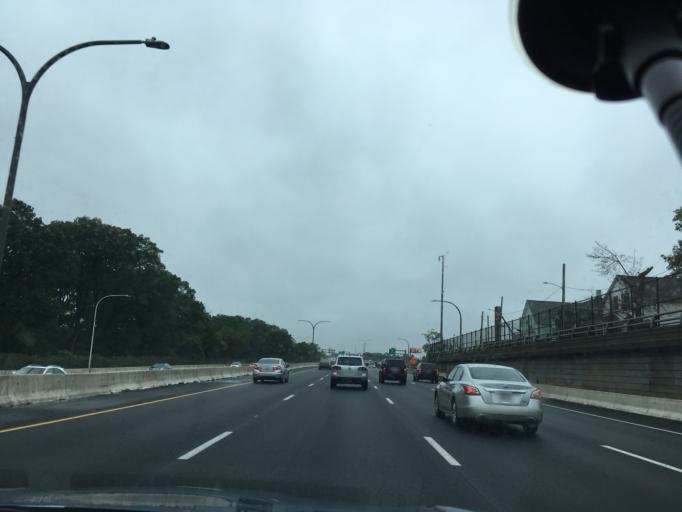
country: US
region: Rhode Island
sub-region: Providence County
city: Cranston
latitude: 41.7929
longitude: -71.4124
